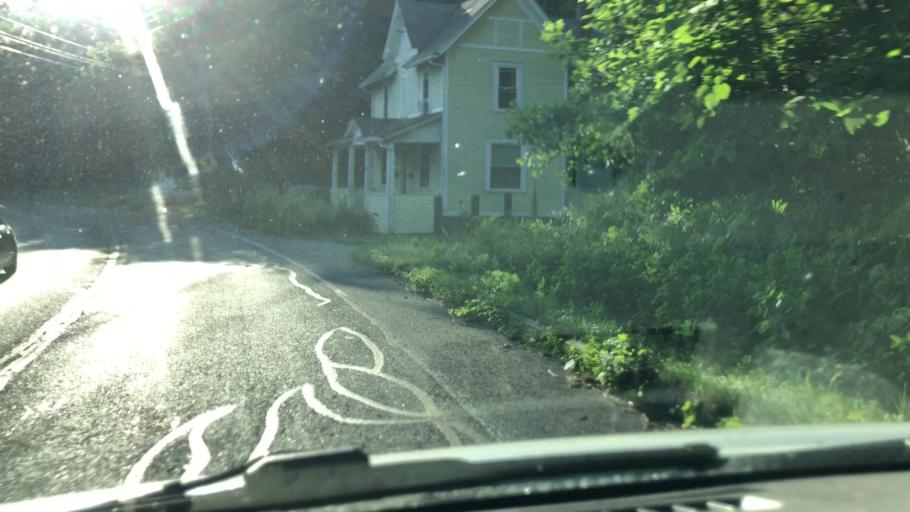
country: US
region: Massachusetts
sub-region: Franklin County
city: Greenfield
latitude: 42.5823
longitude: -72.6073
